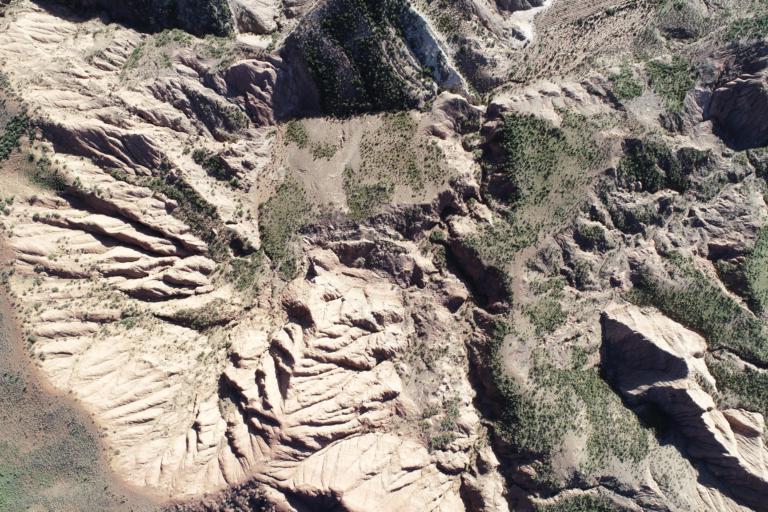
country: BO
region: La Paz
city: Curahuara de Carangas
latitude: -17.3046
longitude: -68.4985
